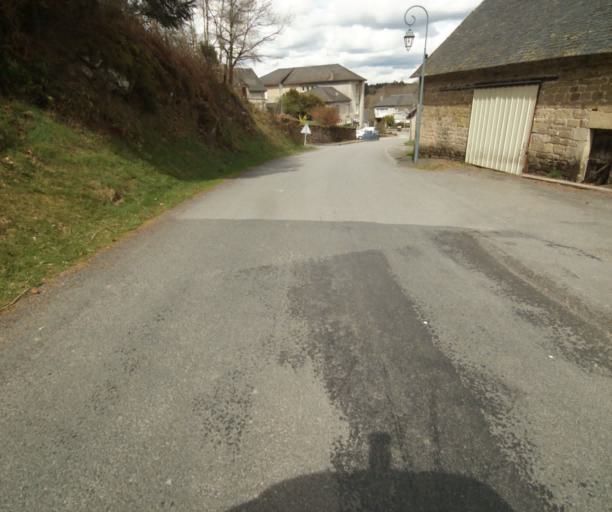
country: FR
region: Limousin
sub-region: Departement de la Correze
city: Correze
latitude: 45.3758
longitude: 1.9362
